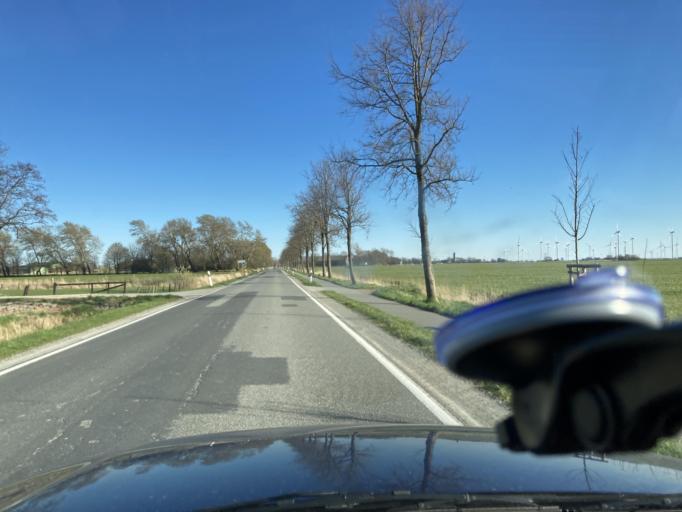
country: DE
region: Schleswig-Holstein
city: Neuenkirchen
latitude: 54.2361
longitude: 9.0057
